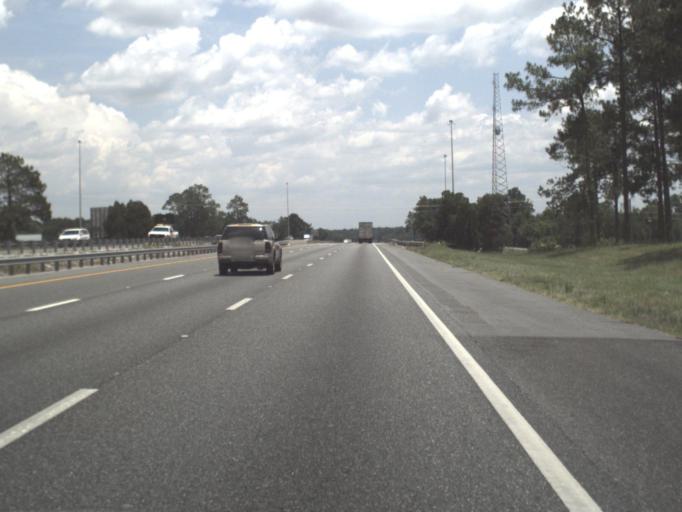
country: US
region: Florida
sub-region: Hamilton County
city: Jasper
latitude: 30.5190
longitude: -83.0601
